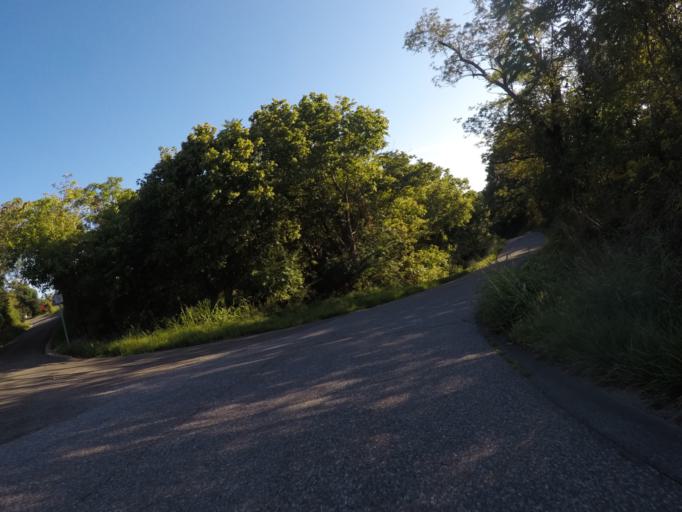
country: US
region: Ohio
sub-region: Lawrence County
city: Burlington
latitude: 38.5264
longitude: -82.5257
